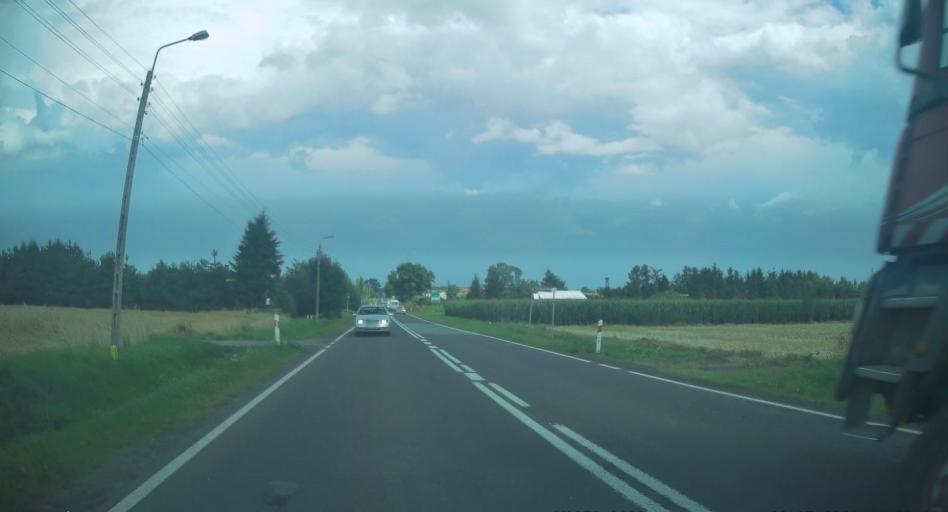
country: PL
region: Lodz Voivodeship
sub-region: Powiat brzezinski
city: Jezow
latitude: 51.8122
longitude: 19.9488
